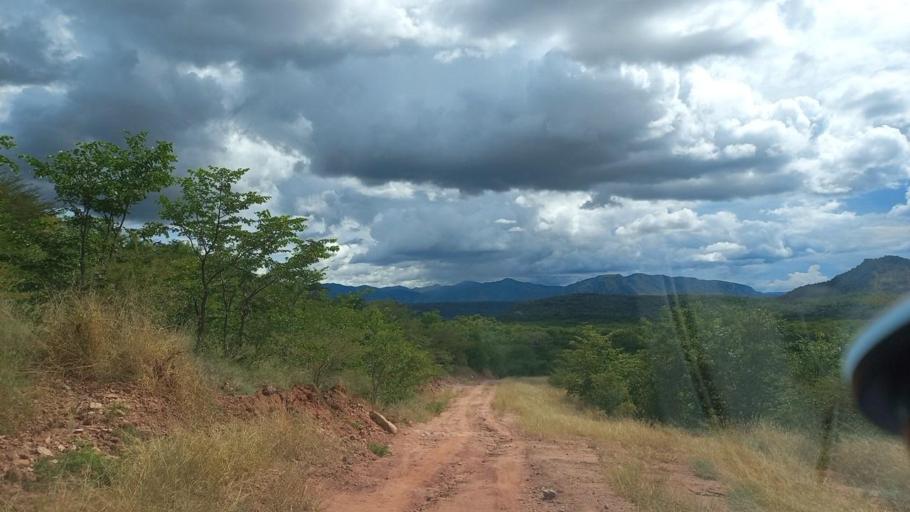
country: ZM
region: Lusaka
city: Luangwa
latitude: -15.6354
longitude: 30.3848
